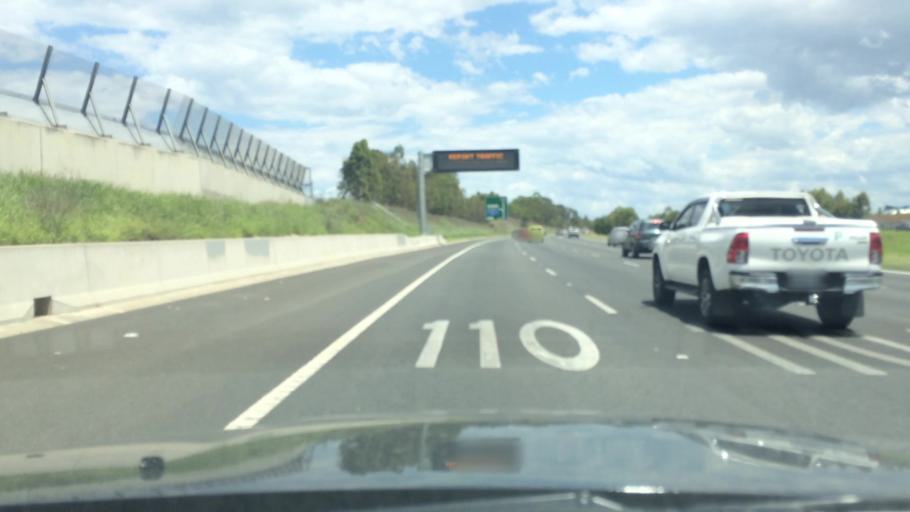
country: AU
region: New South Wales
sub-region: Campbelltown Municipality
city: Glenfield
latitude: -33.9723
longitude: 150.8736
